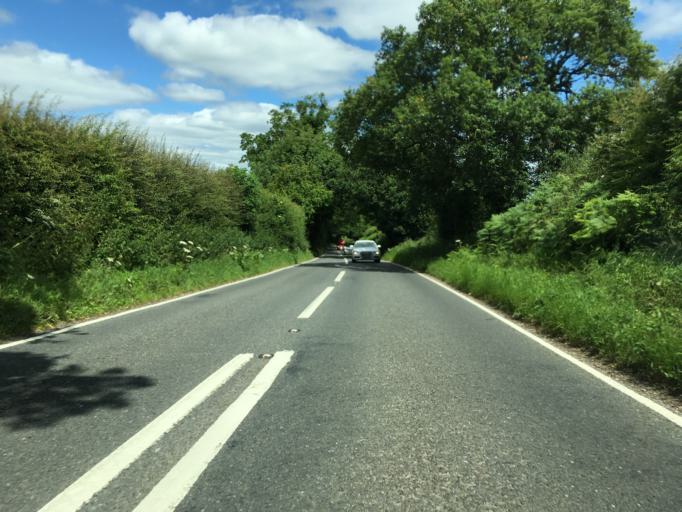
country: GB
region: England
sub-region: Hampshire
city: Highclere
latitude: 51.3218
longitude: -1.3823
